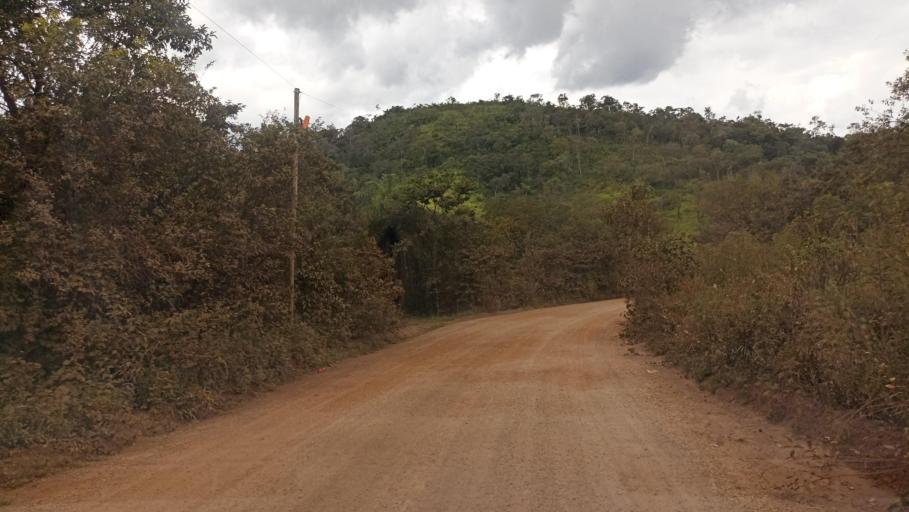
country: BR
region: Minas Gerais
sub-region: Itabirito
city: Itabirito
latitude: -20.3665
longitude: -43.7616
